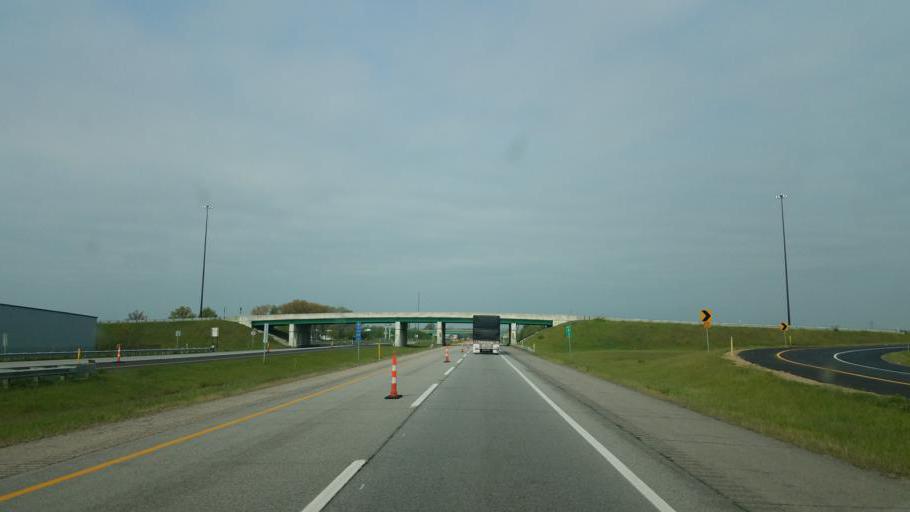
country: US
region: Indiana
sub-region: Elkhart County
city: Simonton Lake
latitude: 41.7311
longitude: -85.9664
